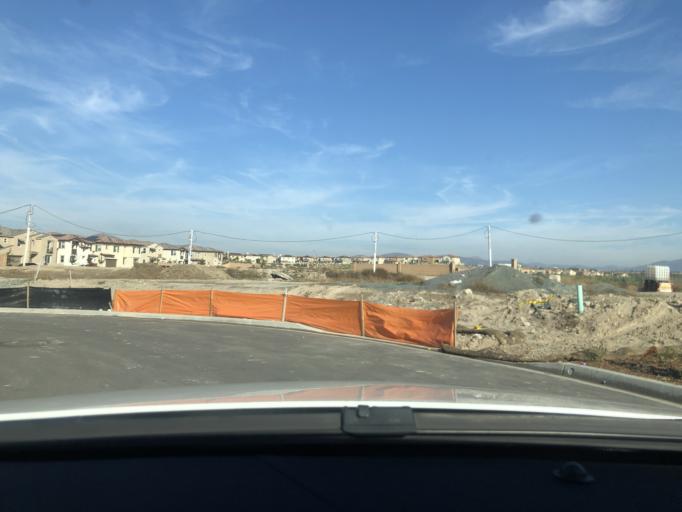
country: US
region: California
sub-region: San Diego County
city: Bonita
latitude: 32.6108
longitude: -116.9902
